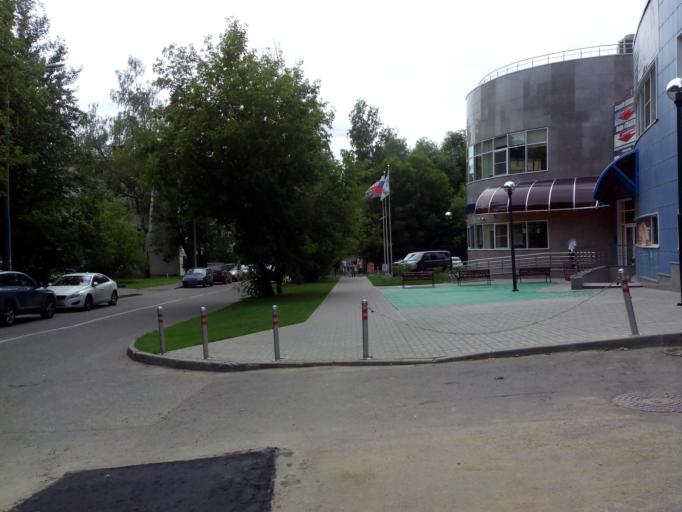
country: RU
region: Moscow
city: Pokrovskoye-Streshnevo
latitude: 55.8196
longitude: 37.4637
